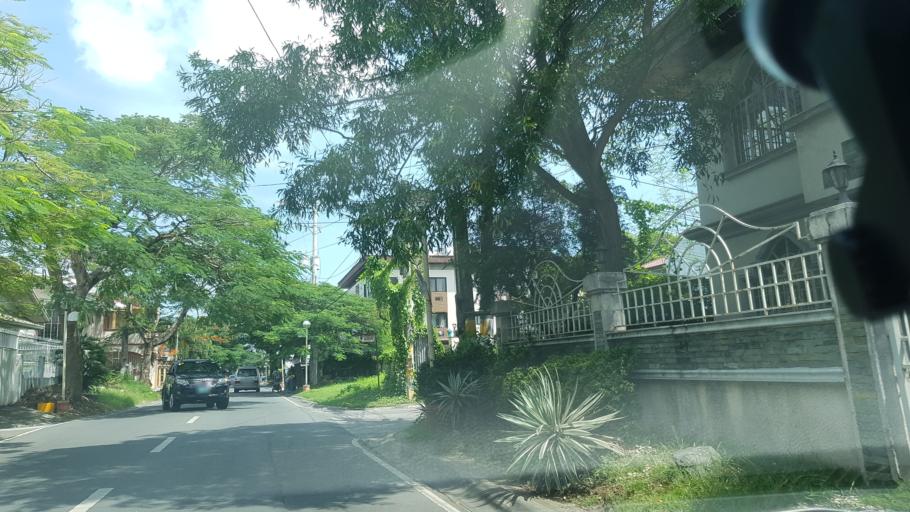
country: PH
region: Calabarzon
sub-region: Province of Rizal
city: Las Pinas
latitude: 14.4282
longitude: 120.9946
